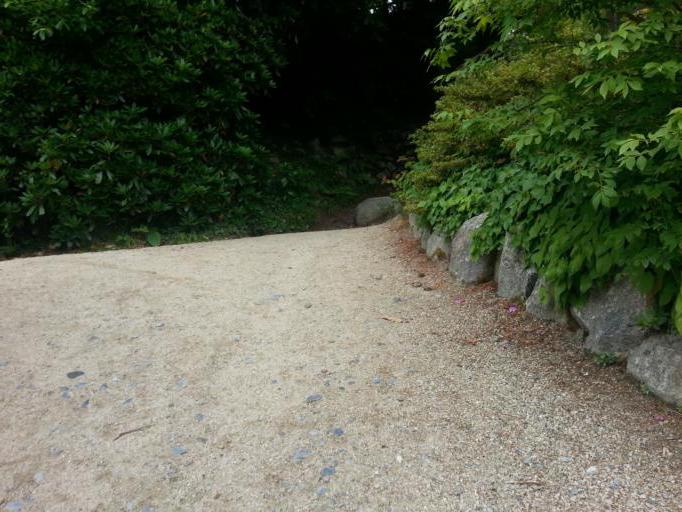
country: IE
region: Leinster
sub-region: Wicklow
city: Enniskerry
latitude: 53.1836
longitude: -6.1824
